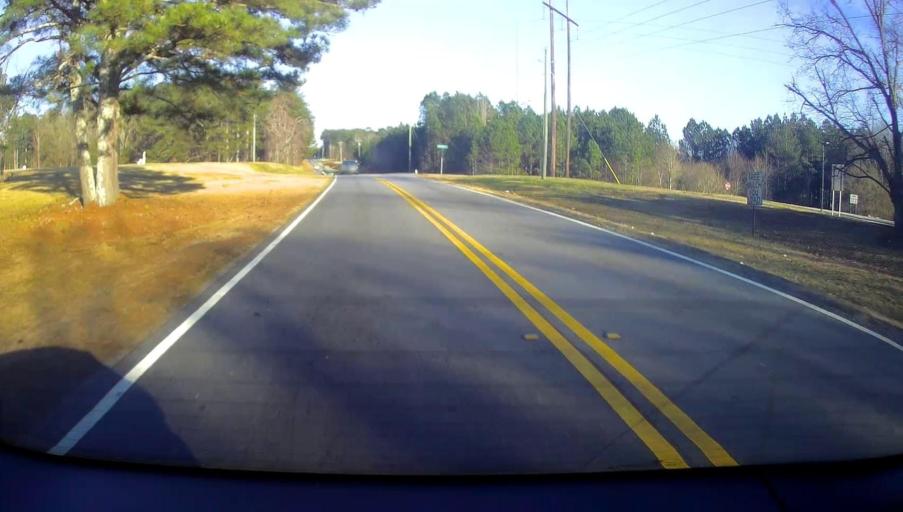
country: US
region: Georgia
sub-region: Fayette County
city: Fayetteville
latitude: 33.4565
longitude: -84.4158
